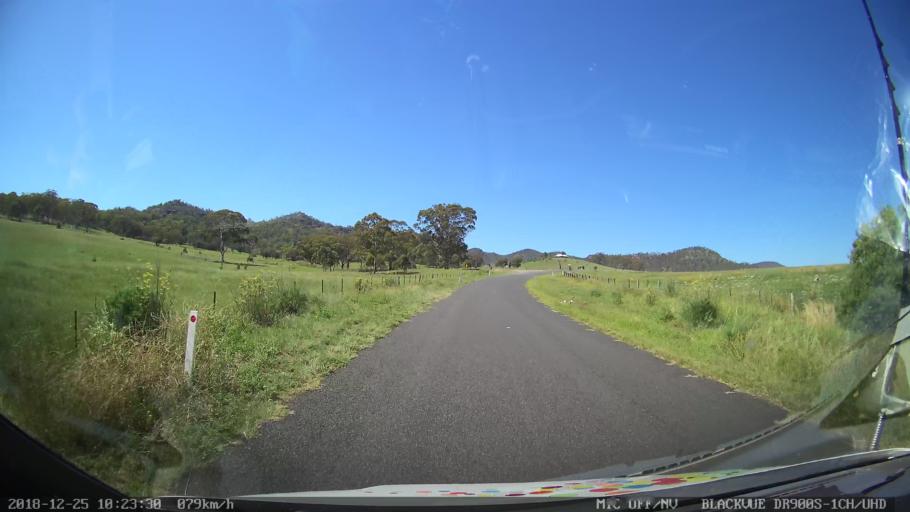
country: AU
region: New South Wales
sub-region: Muswellbrook
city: Denman
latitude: -32.3864
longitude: 150.5227
